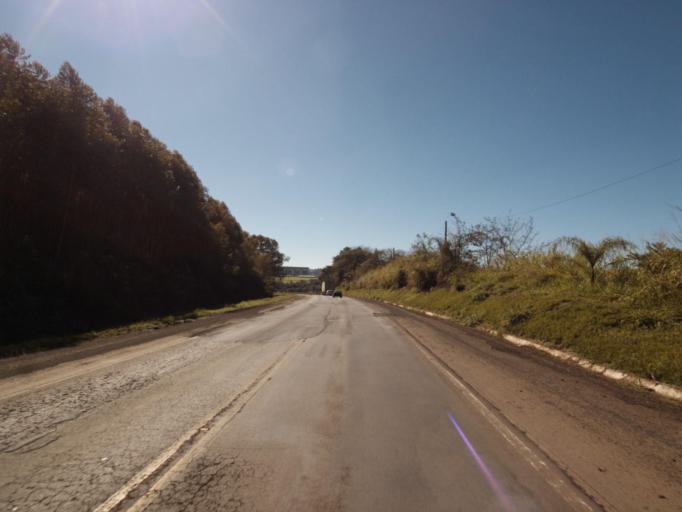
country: BR
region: Rio Grande do Sul
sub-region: Frederico Westphalen
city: Frederico Westphalen
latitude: -26.9152
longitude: -53.1891
